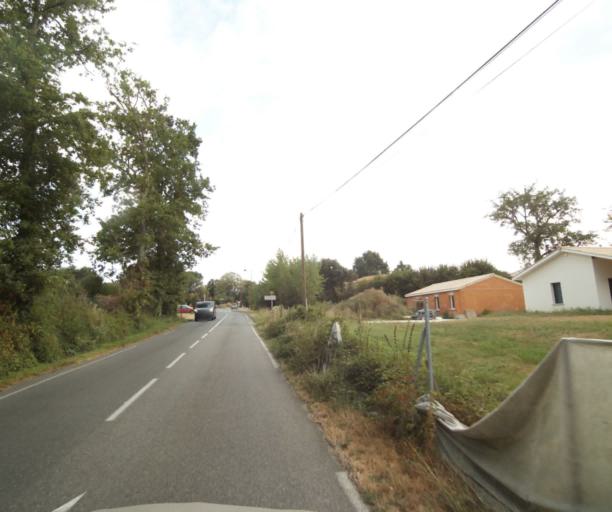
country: FR
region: Aquitaine
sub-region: Departement de la Gironde
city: Creon
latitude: 44.7675
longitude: -0.3595
